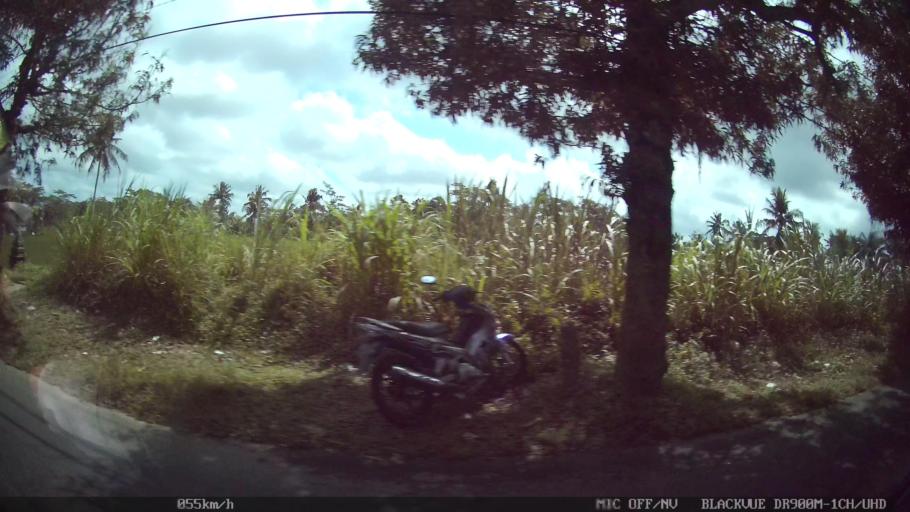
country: ID
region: Bali
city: Banjar Mulung
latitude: -8.4889
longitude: 115.3204
